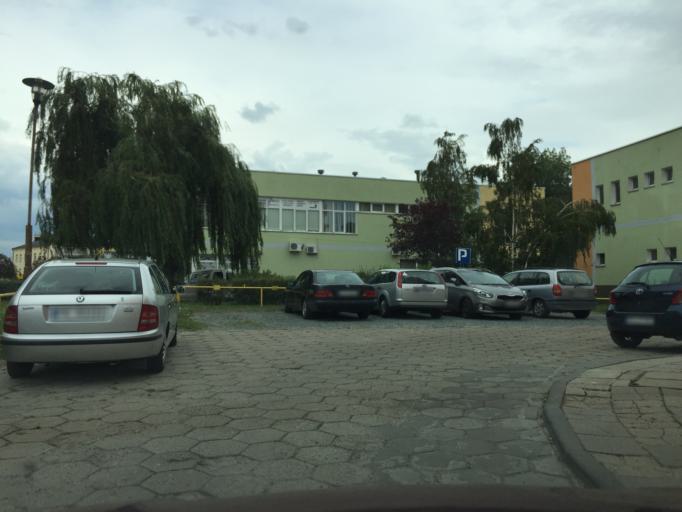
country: PL
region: Greater Poland Voivodeship
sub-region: Kalisz
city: Kalisz
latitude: 51.7471
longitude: 18.0707
